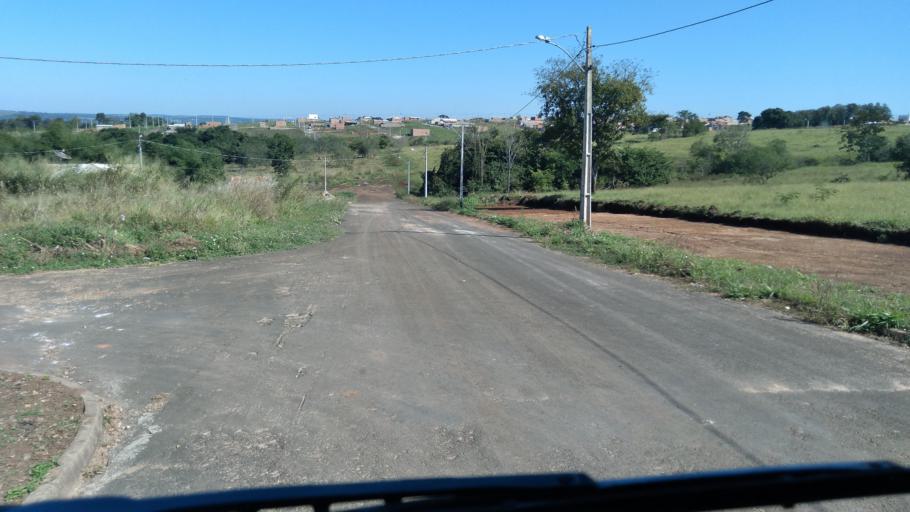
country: BR
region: Goias
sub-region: Mineiros
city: Mineiros
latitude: -17.5757
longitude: -52.5771
